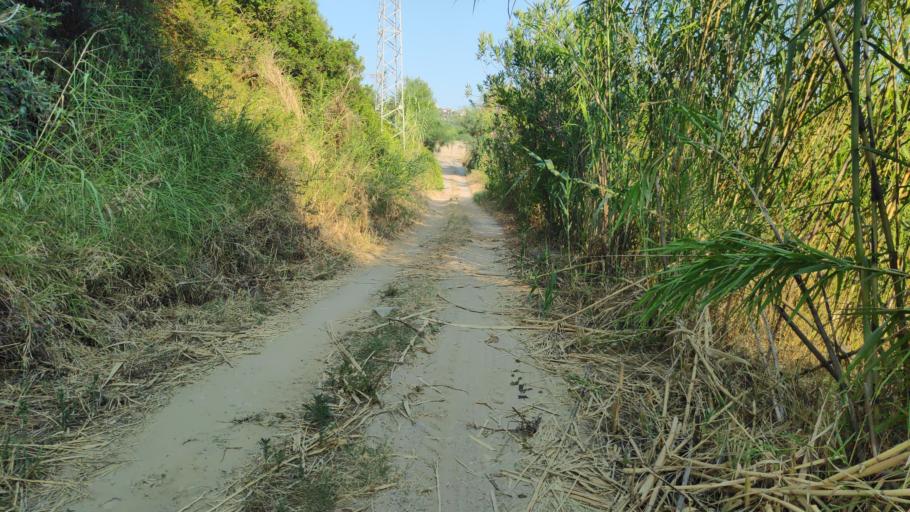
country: IT
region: Calabria
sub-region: Provincia di Reggio Calabria
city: Placanica
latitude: 38.4137
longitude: 16.4401
